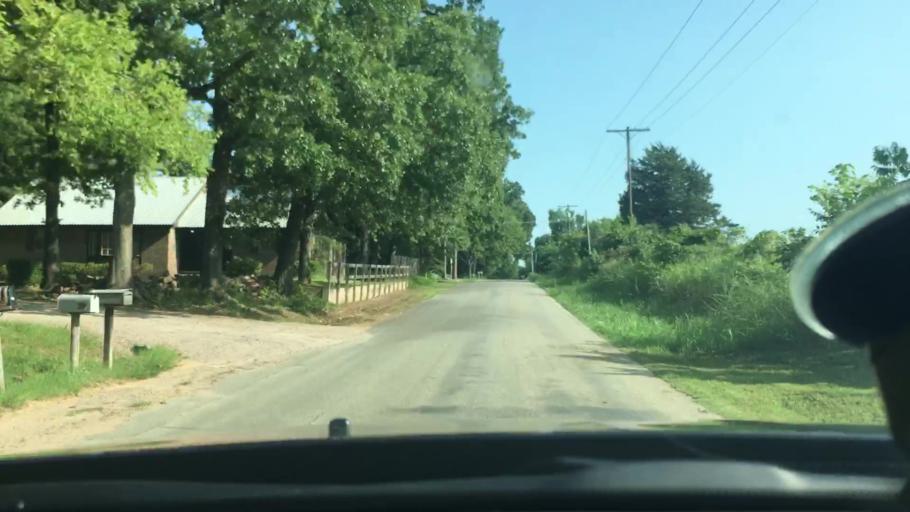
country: US
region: Oklahoma
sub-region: Johnston County
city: Tishomingo
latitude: 34.2248
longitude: -96.6710
